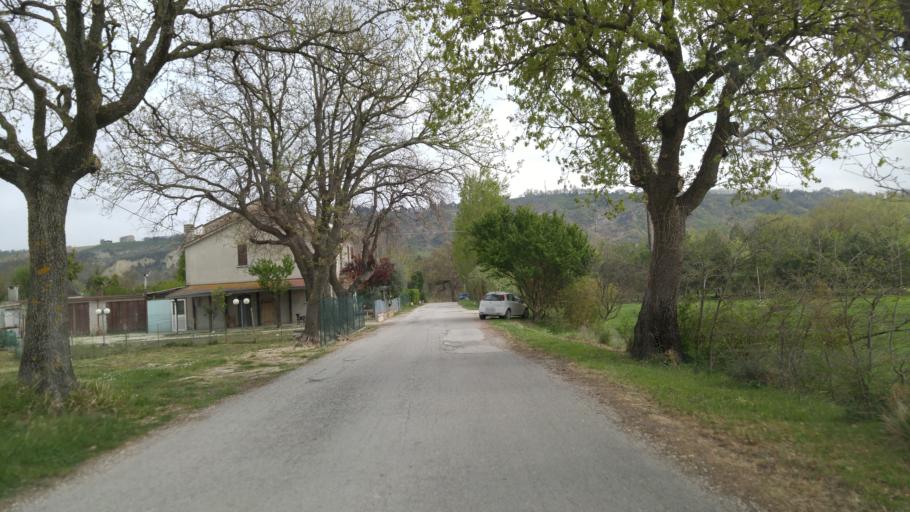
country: IT
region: The Marches
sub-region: Provincia di Pesaro e Urbino
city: Bellocchi
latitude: 43.7729
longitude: 12.9877
